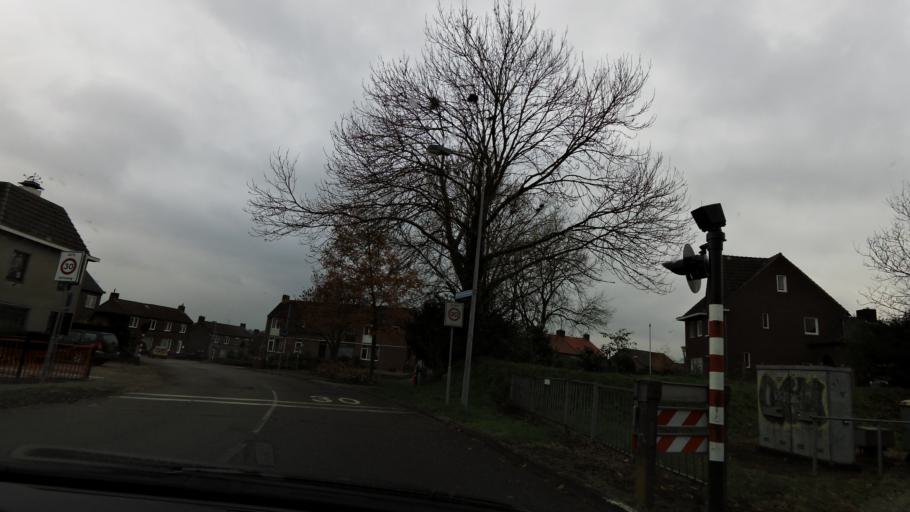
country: NL
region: Limburg
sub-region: Gemeente Voerendaal
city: Klimmen
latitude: 50.8657
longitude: 5.8889
